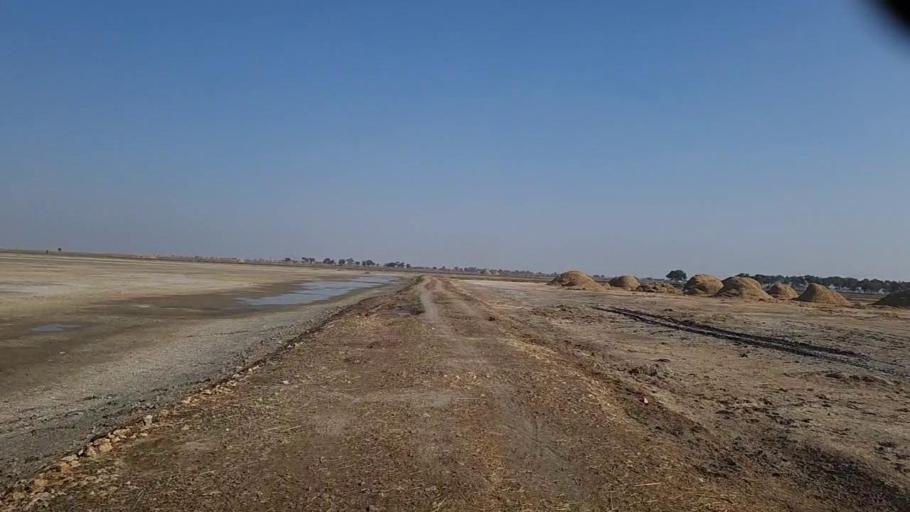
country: PK
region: Sindh
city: Thul
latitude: 28.3589
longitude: 68.7717
